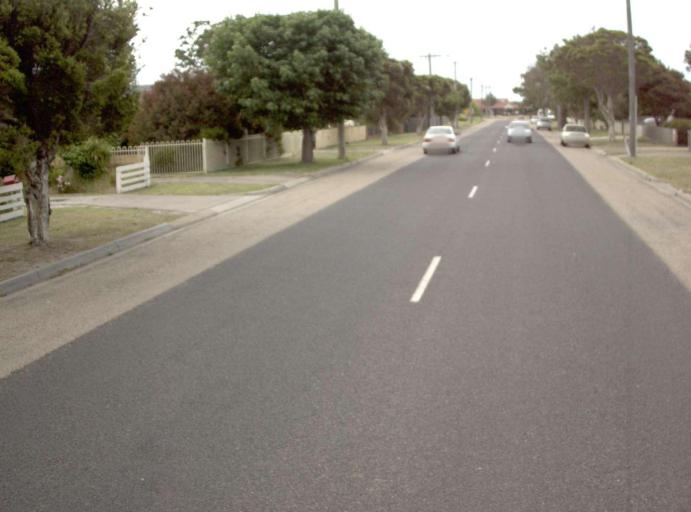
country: AU
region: Victoria
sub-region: East Gippsland
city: Bairnsdale
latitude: -37.9098
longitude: 147.7203
